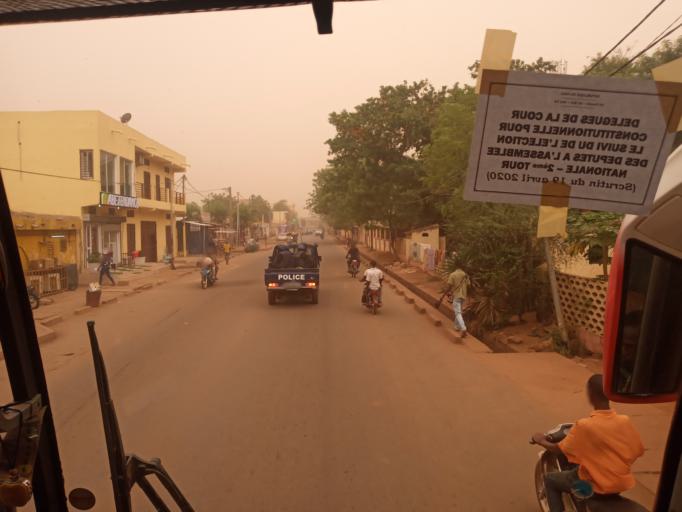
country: ML
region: Bamako
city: Bamako
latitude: 12.6474
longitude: -8.0053
